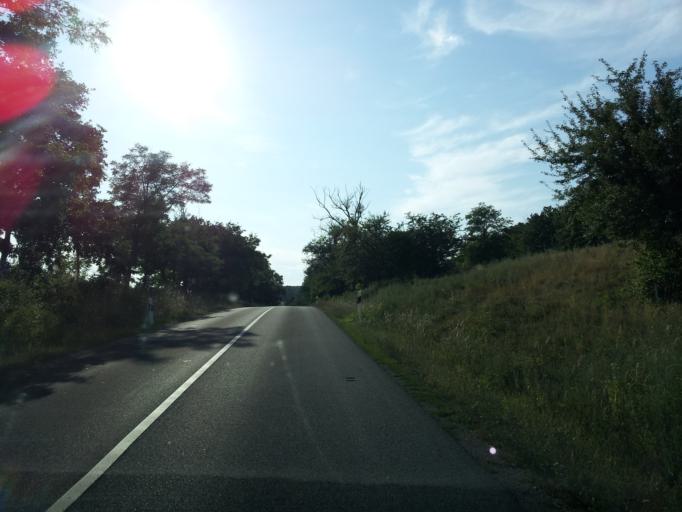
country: HU
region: Veszprem
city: Urkut
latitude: 47.0010
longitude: 17.6463
